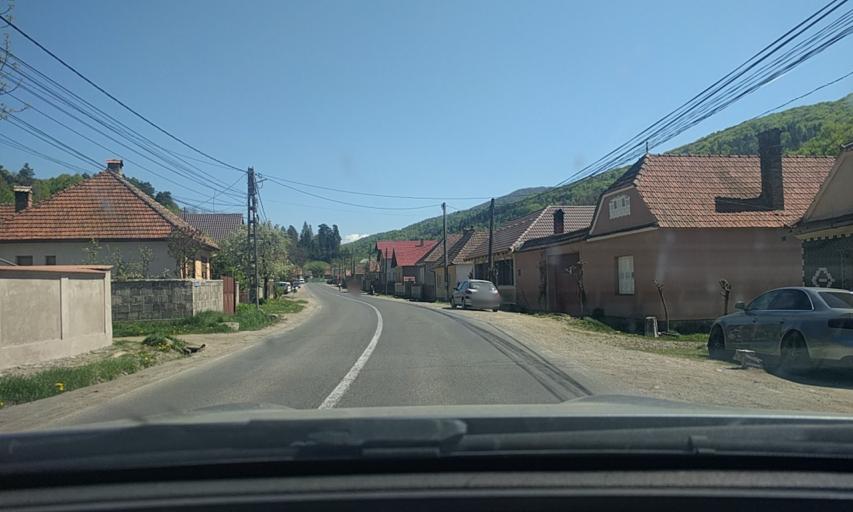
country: RO
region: Brasov
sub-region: Comuna Teliu
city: Teliu
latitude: 45.6937
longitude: 25.8727
